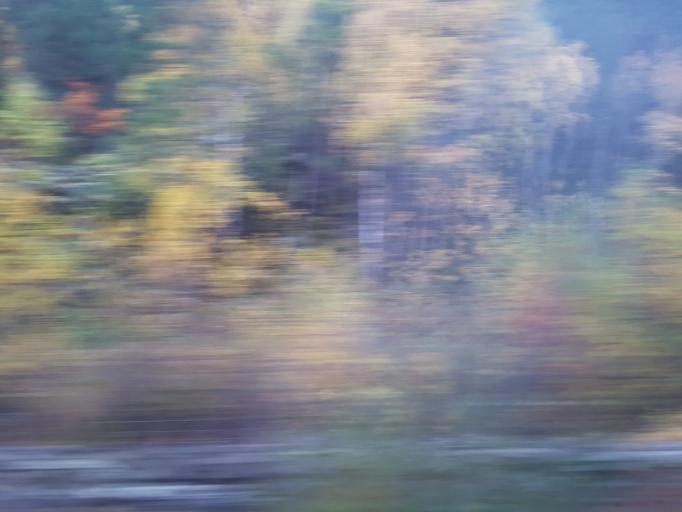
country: NO
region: Oppland
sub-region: Sel
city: Otta
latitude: 61.8396
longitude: 9.4547
